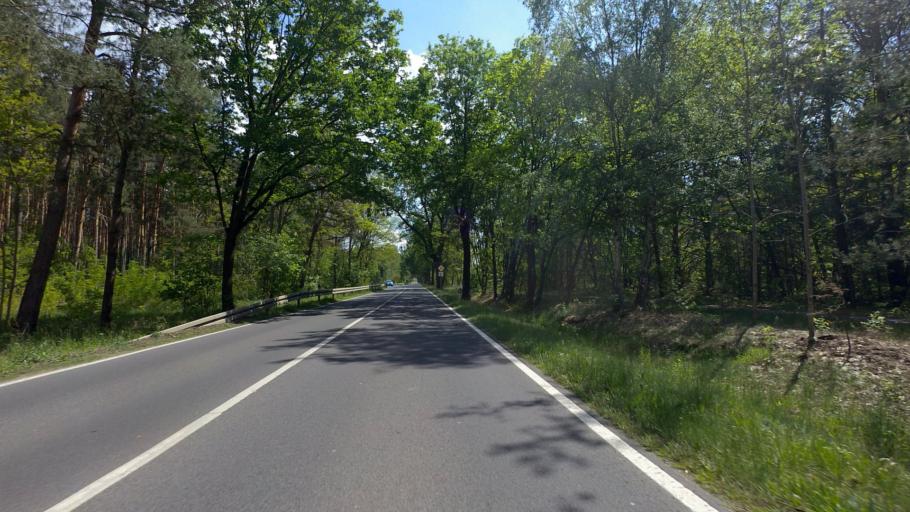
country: DE
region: Brandenburg
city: Luebben
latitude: 51.9441
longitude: 13.9698
